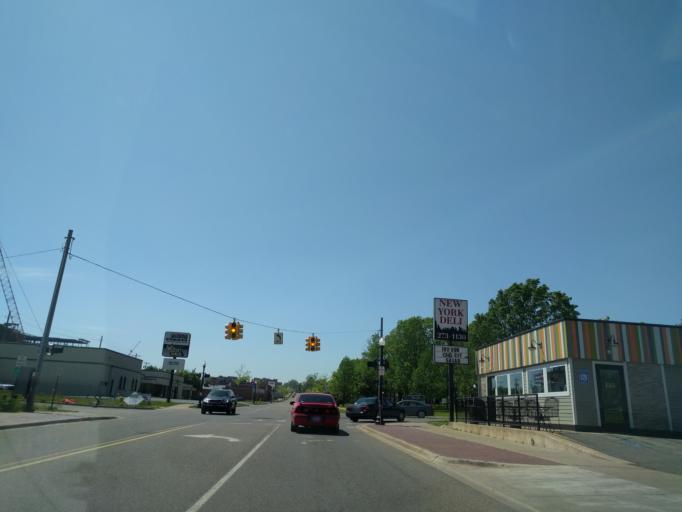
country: US
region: Michigan
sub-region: Marquette County
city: Marquette
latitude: 46.5448
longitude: -87.4035
